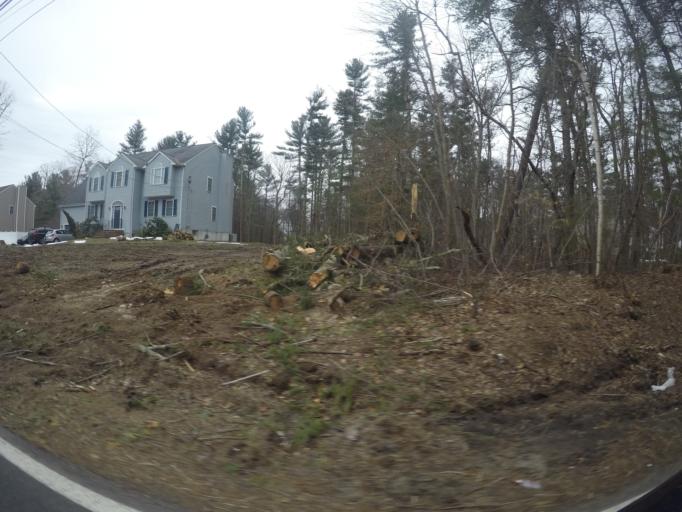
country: US
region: Massachusetts
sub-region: Bristol County
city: Easton
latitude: 42.0201
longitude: -71.1087
